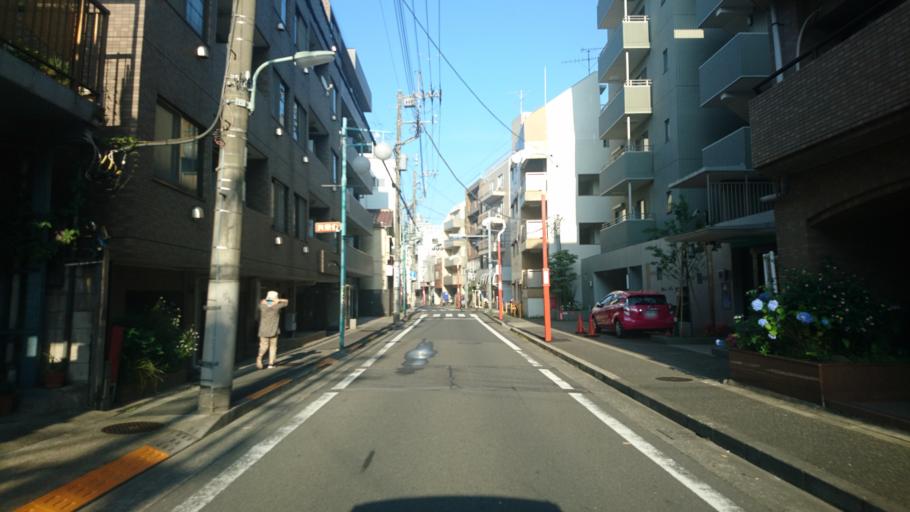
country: JP
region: Kanagawa
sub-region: Kawasaki-shi
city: Kawasaki
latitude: 35.6022
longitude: 139.7148
